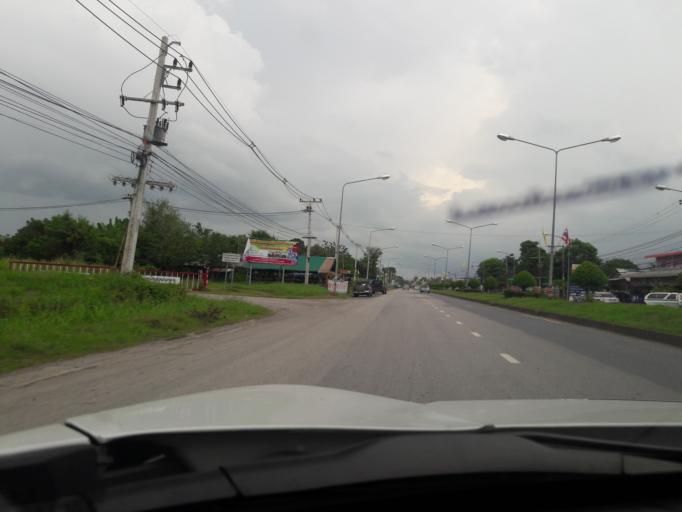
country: TH
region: Lop Buri
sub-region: Amphoe Tha Luang
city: Tha Luang
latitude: 15.0689
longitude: 101.1146
